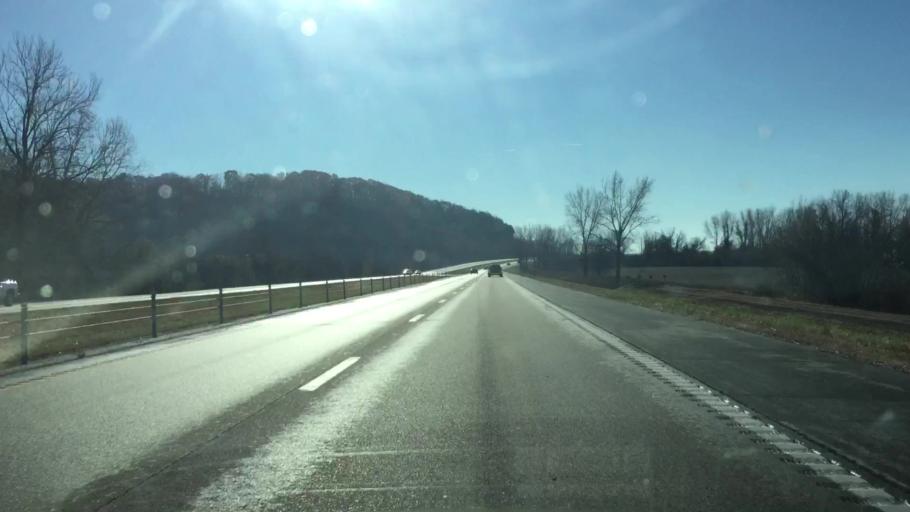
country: US
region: Missouri
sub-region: Cole County
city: Jefferson City
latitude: 38.6414
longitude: -92.1996
